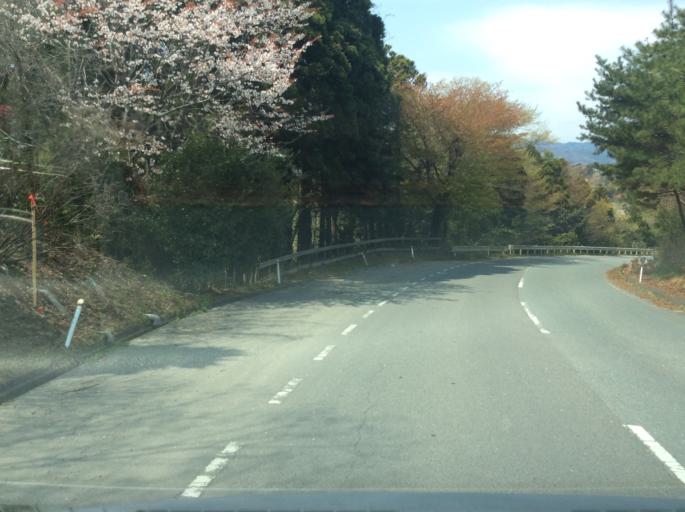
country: JP
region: Fukushima
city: Namie
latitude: 37.2714
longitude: 141.0076
